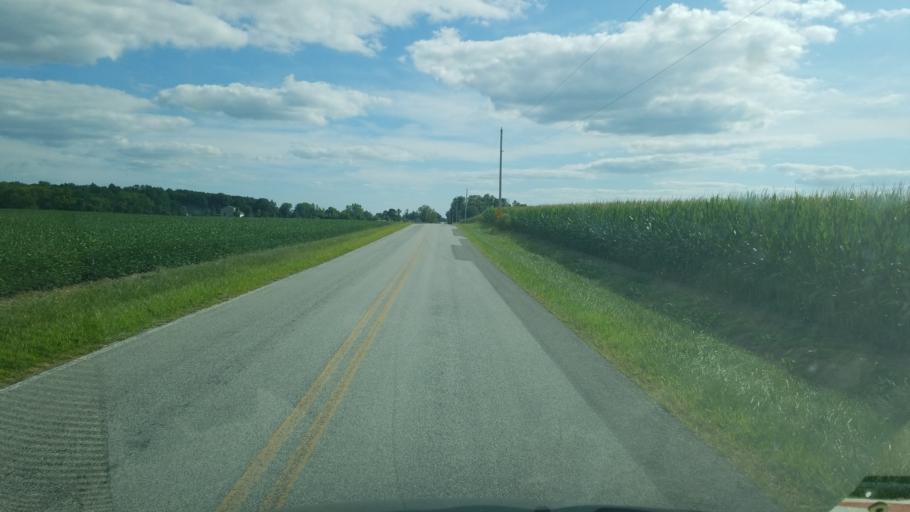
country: US
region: Ohio
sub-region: Champaign County
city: Saint Paris
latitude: 40.2173
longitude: -83.9413
